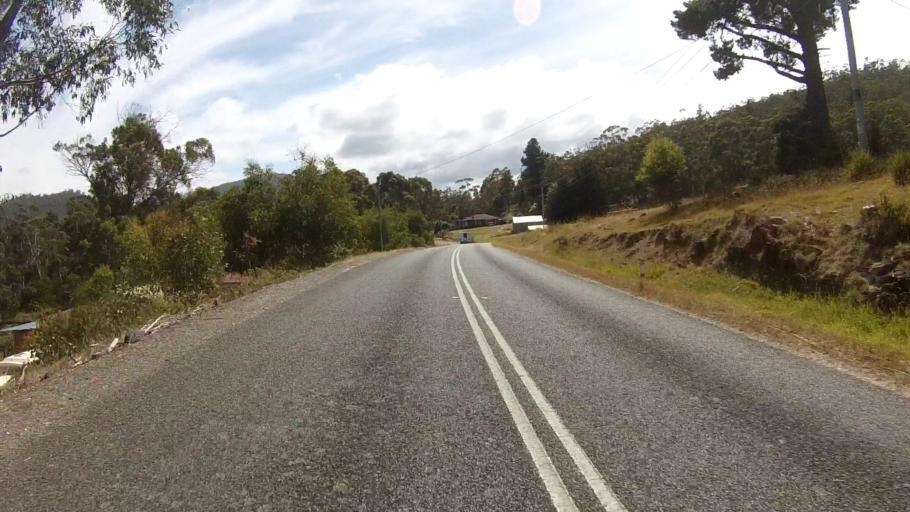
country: AU
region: Tasmania
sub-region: Huon Valley
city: Cygnet
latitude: -43.2446
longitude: 147.1500
